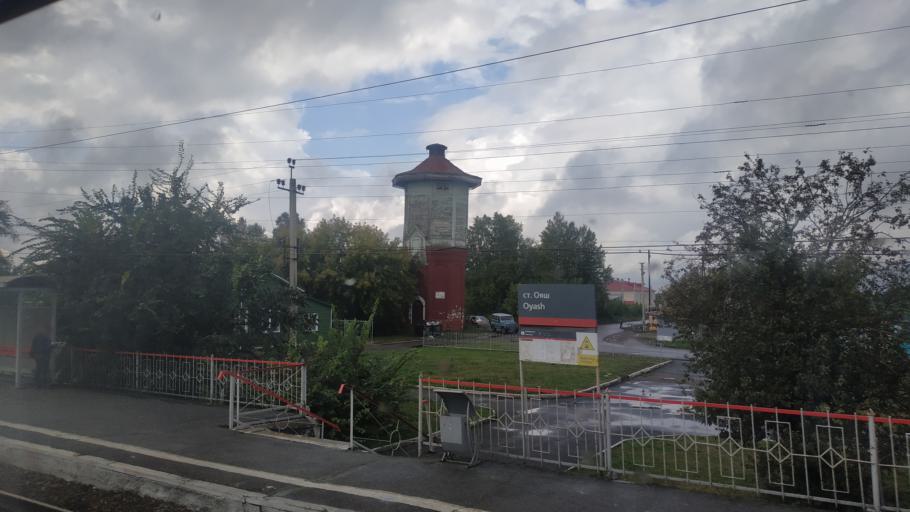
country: RU
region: Novosibirsk
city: Stantsionno-Oyashinskiy
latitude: 55.4624
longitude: 83.8205
